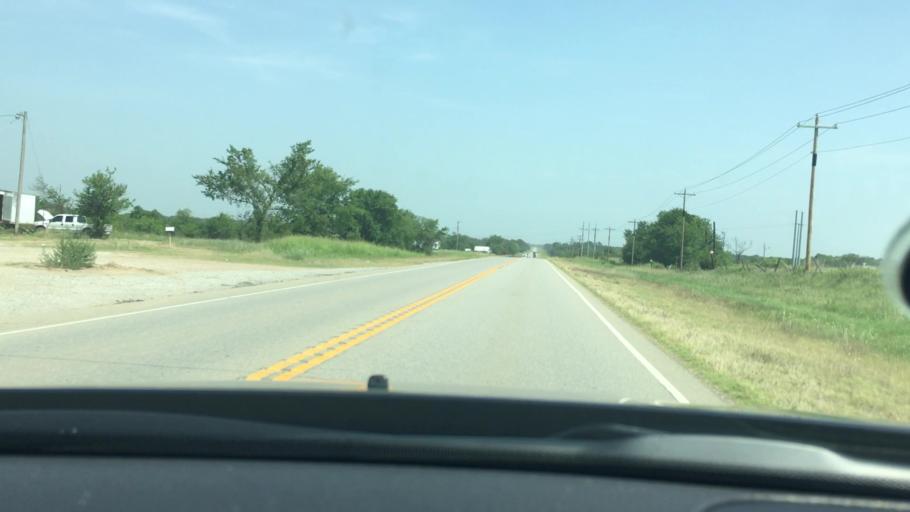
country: US
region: Oklahoma
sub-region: Coal County
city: Coalgate
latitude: 34.4807
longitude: -96.2182
